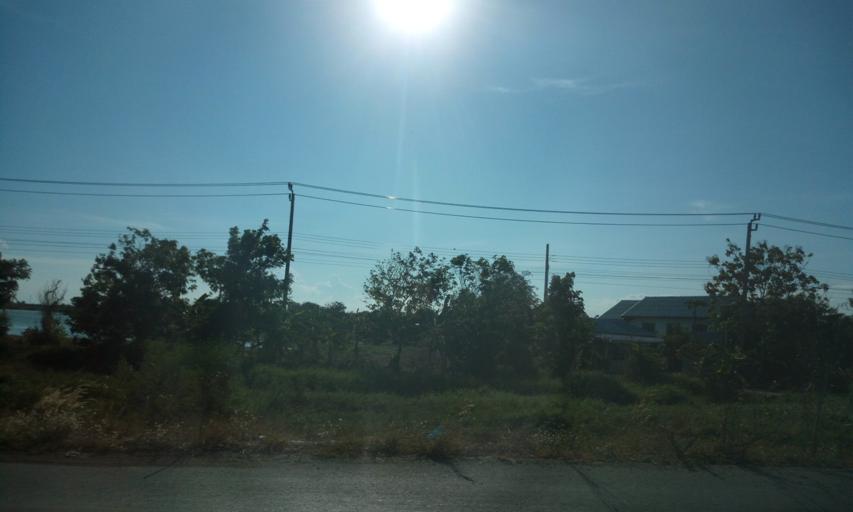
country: TH
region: Samut Prakan
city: Bang Bo District
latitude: 13.5699
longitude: 100.7561
